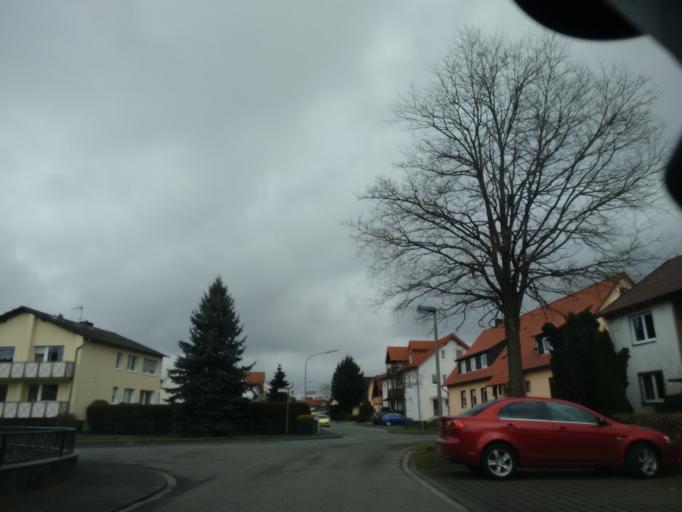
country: DE
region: North Rhine-Westphalia
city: Bad Lippspringe
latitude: 51.7730
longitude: 8.8079
